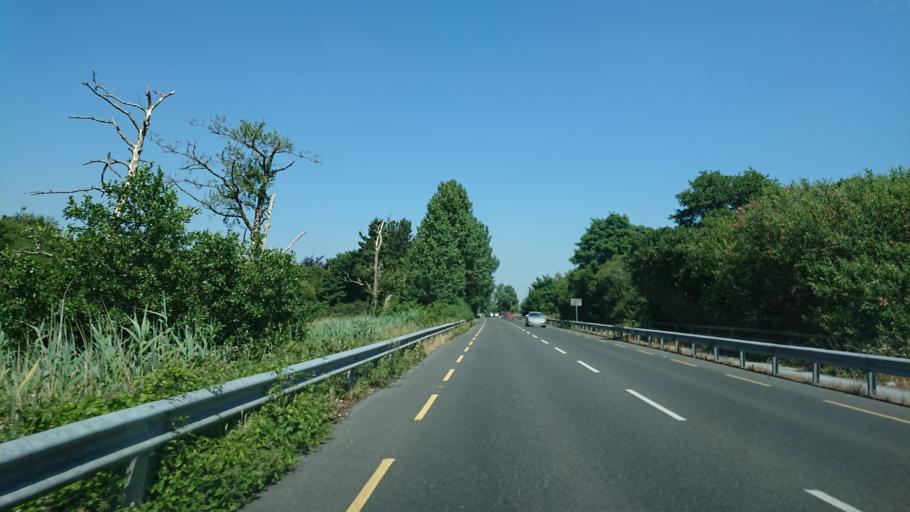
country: IE
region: Munster
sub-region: Waterford
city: Waterford
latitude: 52.2269
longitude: -7.1248
